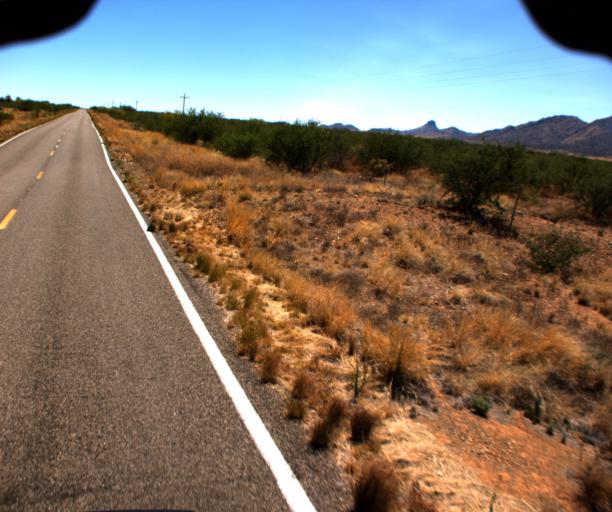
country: US
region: Arizona
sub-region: Pima County
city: Three Points
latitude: 31.7687
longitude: -111.4692
